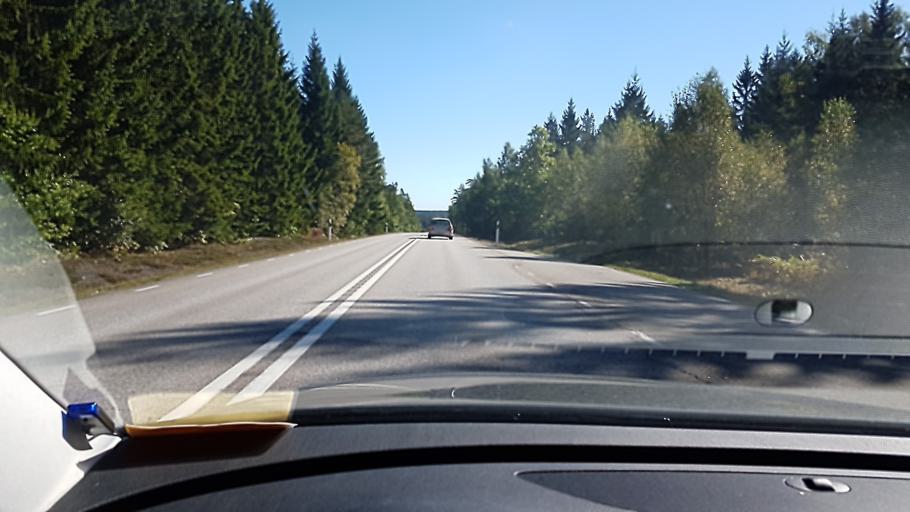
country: SE
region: Kronoberg
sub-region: Lessebo Kommun
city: Lessebo
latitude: 56.7297
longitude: 15.3550
